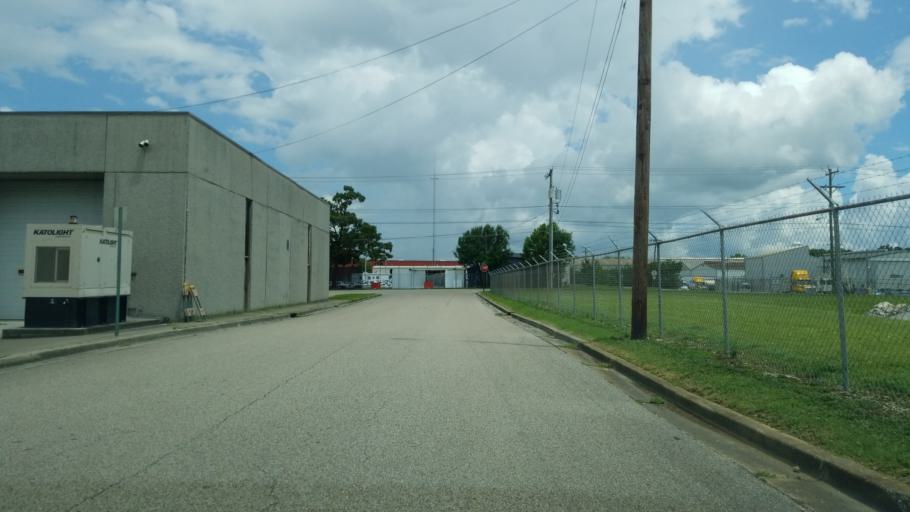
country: US
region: Tennessee
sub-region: Hamilton County
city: East Chattanooga
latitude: 35.0799
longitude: -85.2628
